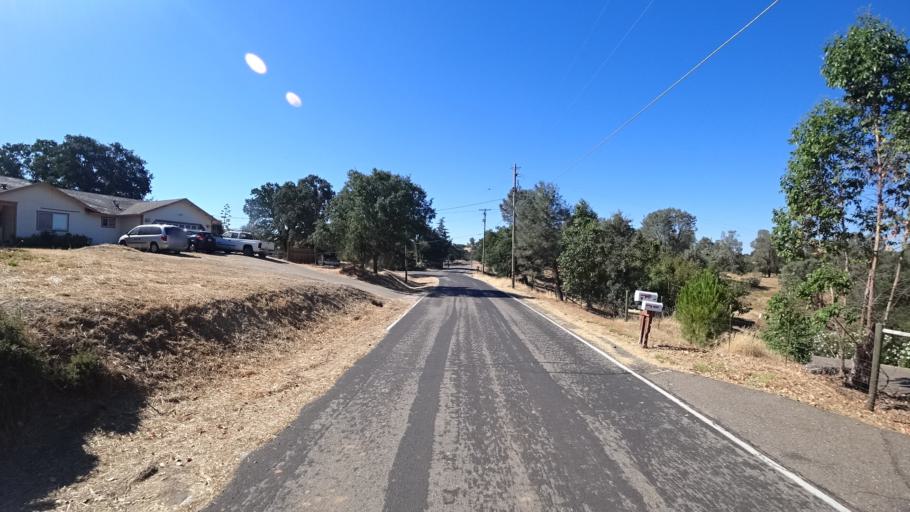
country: US
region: California
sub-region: Calaveras County
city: Rancho Calaveras
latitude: 38.0917
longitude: -120.8610
